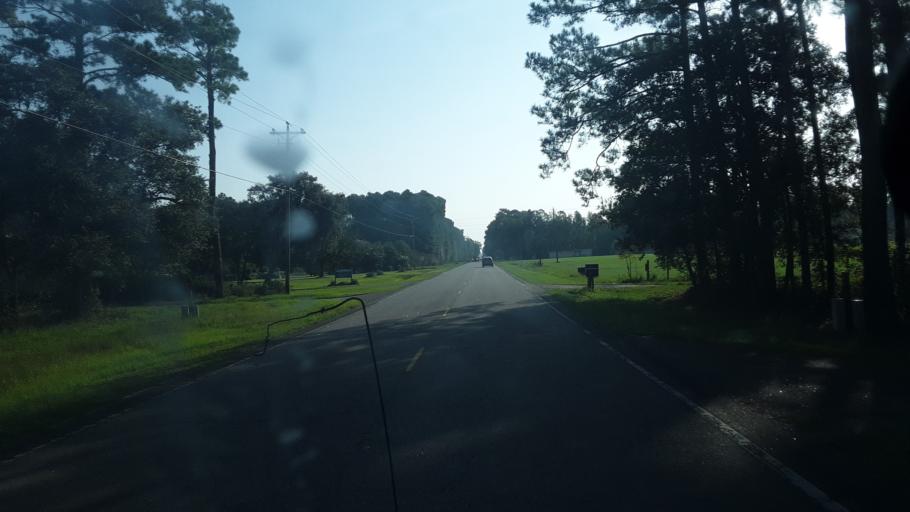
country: US
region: South Carolina
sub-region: Horry County
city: Forestbrook
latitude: 33.8382
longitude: -78.8730
